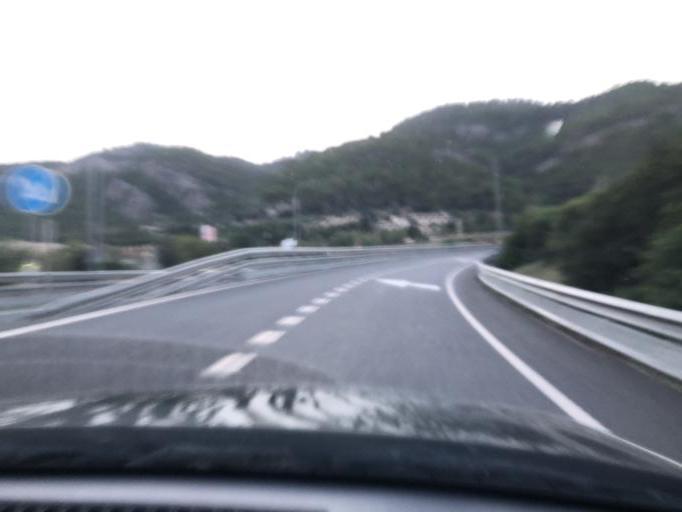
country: ES
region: Balearic Islands
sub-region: Illes Balears
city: Andratx
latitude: 39.5671
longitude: 2.4216
